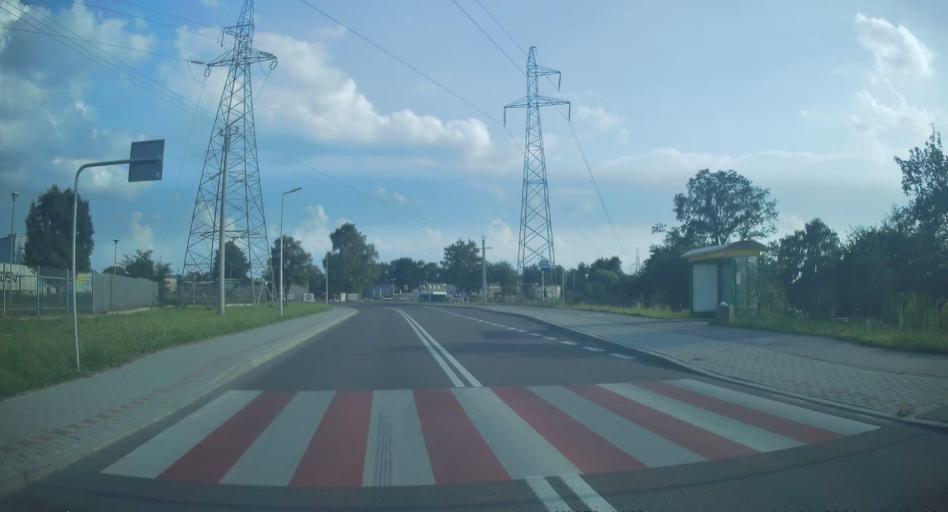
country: PL
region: Subcarpathian Voivodeship
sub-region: Powiat debicki
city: Debica
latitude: 50.0443
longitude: 21.3806
